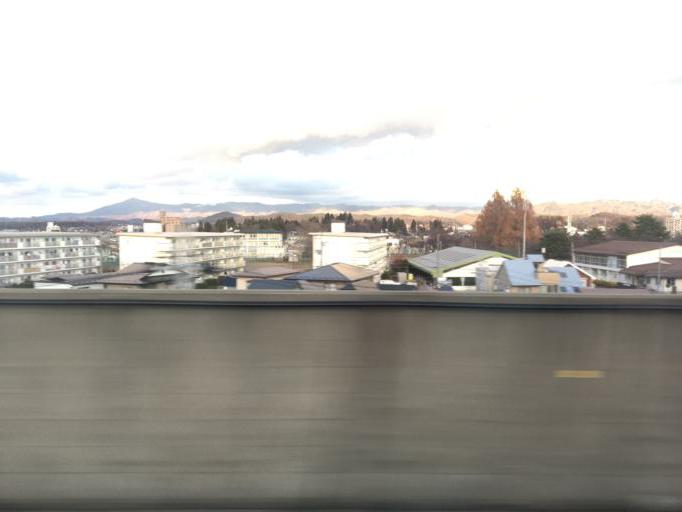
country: JP
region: Iwate
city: Morioka-shi
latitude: 39.7171
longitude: 141.1194
